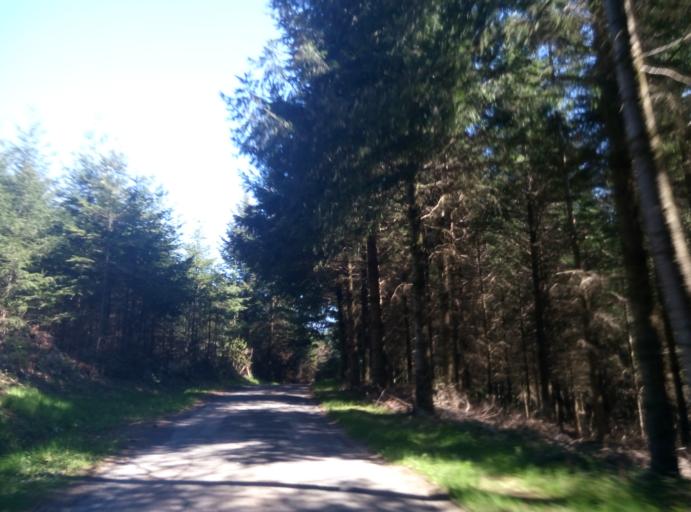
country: FR
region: Rhone-Alpes
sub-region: Departement du Rhone
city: Cublize
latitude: 45.9997
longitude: 4.4174
